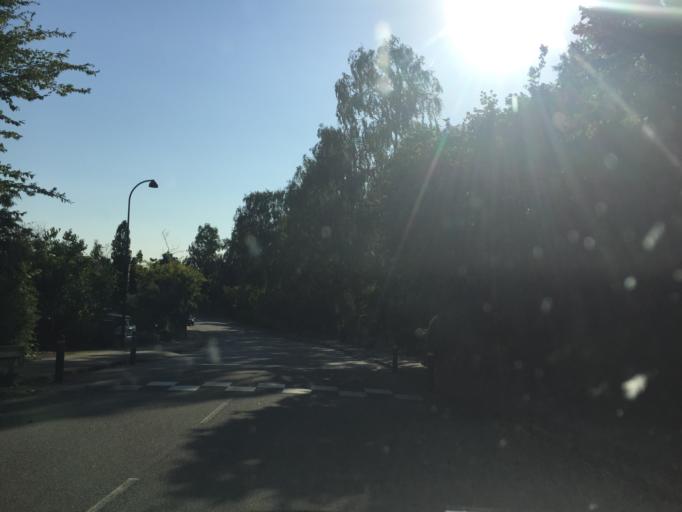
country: DK
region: Capital Region
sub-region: Lyngby-Tarbaek Kommune
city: Kongens Lyngby
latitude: 55.7656
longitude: 12.5309
